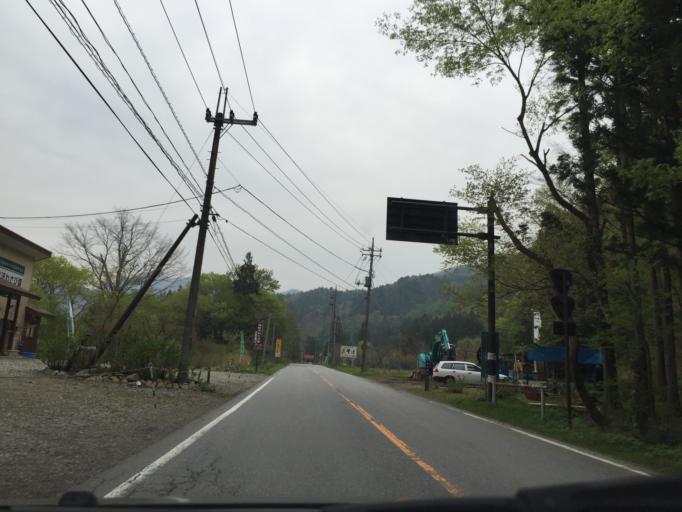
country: JP
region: Tochigi
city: Nikko
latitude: 36.9735
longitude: 139.6887
